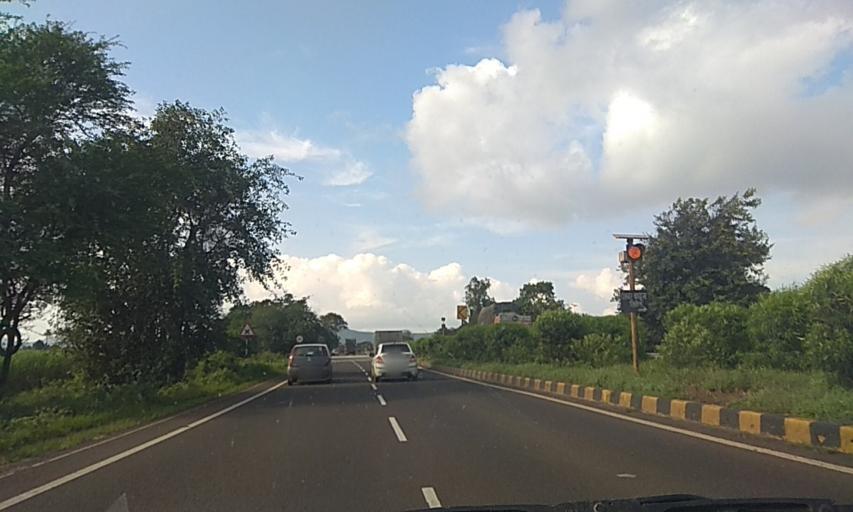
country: IN
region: Maharashtra
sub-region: Kolhapur
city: Kodoli
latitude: 16.9106
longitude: 74.2907
